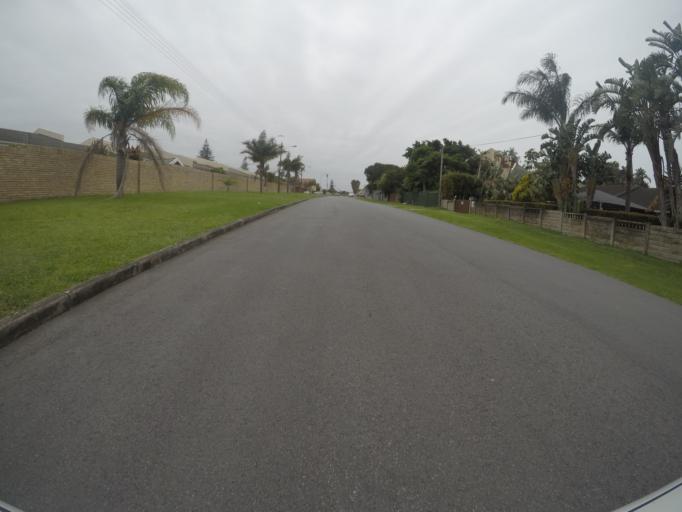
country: ZA
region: Eastern Cape
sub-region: Buffalo City Metropolitan Municipality
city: East London
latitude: -32.9646
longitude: 27.9316
